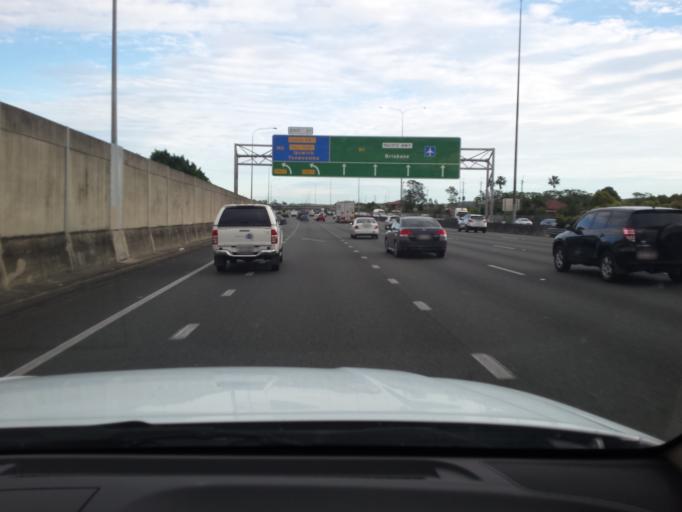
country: AU
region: Queensland
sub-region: Logan
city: Beenleigh
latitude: -27.6942
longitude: 153.1939
